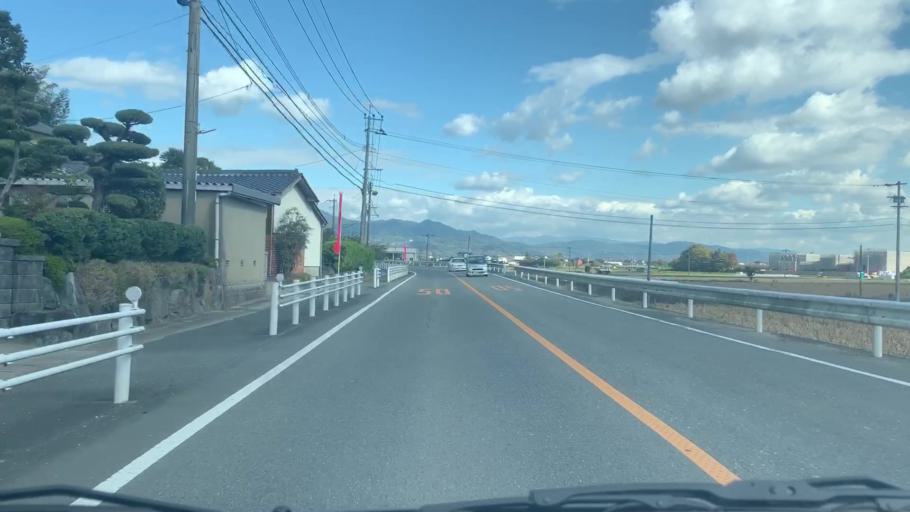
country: JP
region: Saga Prefecture
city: Saga-shi
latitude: 33.2676
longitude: 130.1797
